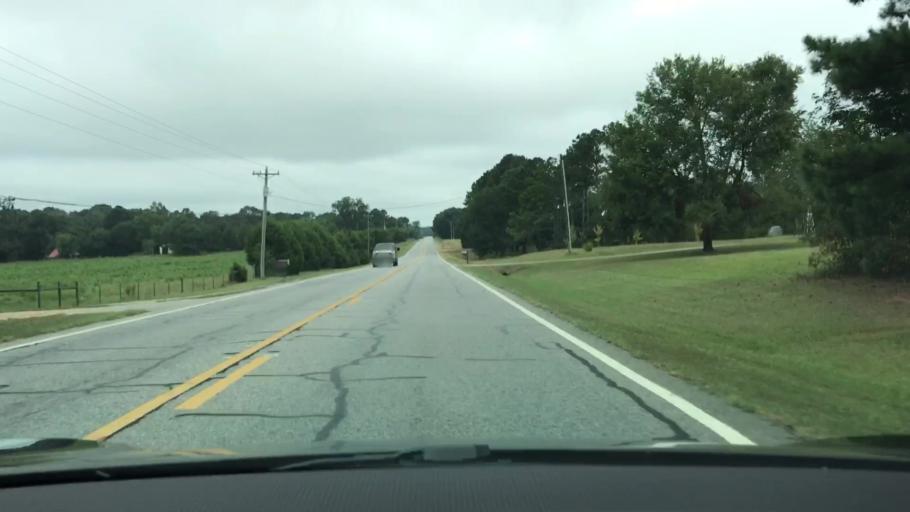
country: US
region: Georgia
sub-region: Oconee County
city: Watkinsville
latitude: 33.7962
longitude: -83.3305
